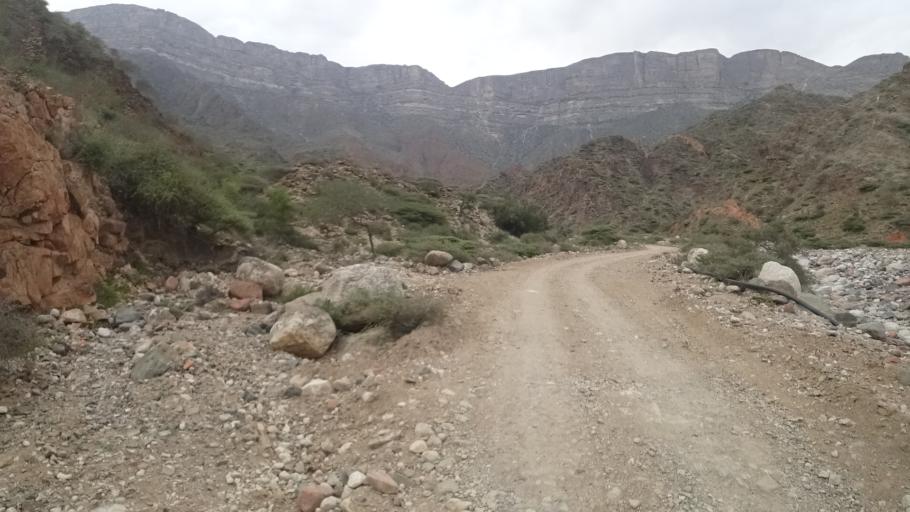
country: OM
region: Zufar
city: Salalah
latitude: 17.1822
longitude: 54.9454
